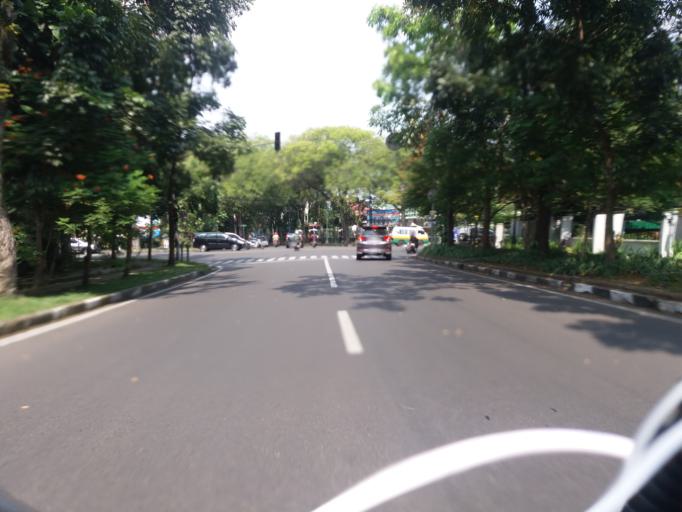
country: ID
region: West Java
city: Bandung
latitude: -6.9117
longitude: 107.6144
